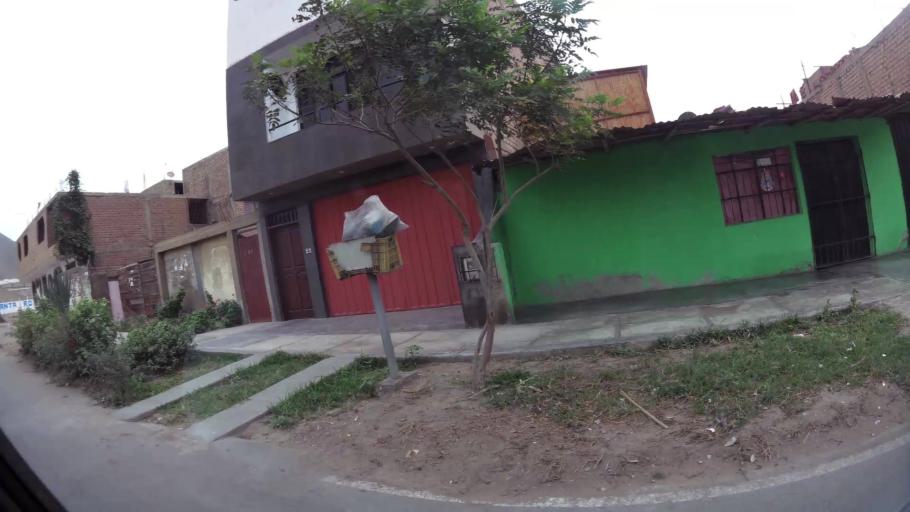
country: PE
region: Lima
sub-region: Lima
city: Santa Rosa
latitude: -11.7856
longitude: -77.1577
